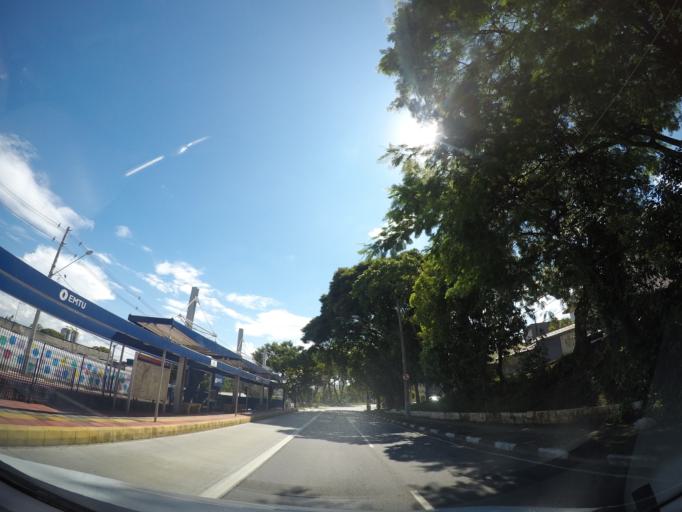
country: BR
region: Sao Paulo
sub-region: Guarulhos
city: Guarulhos
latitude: -23.4555
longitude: -46.5527
